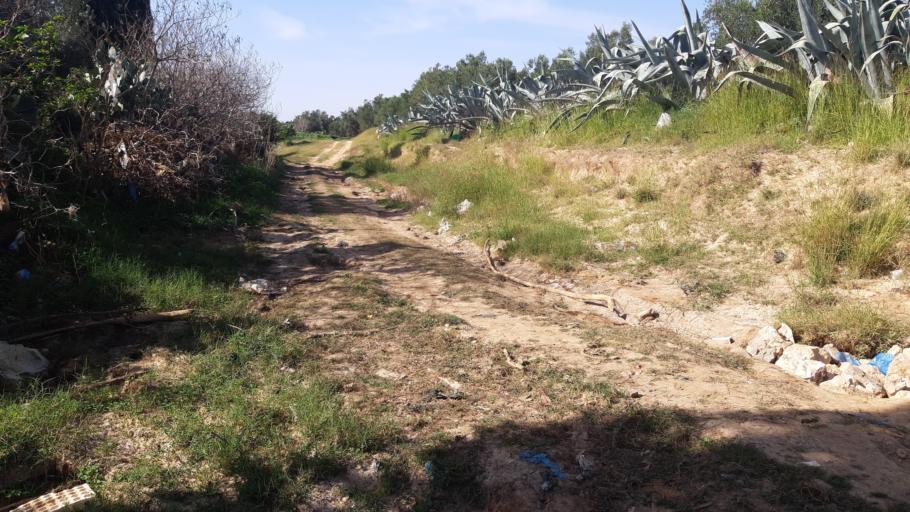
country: TN
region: Al Mahdiyah
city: Sidi `Ulwan
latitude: 35.4308
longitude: 10.9187
